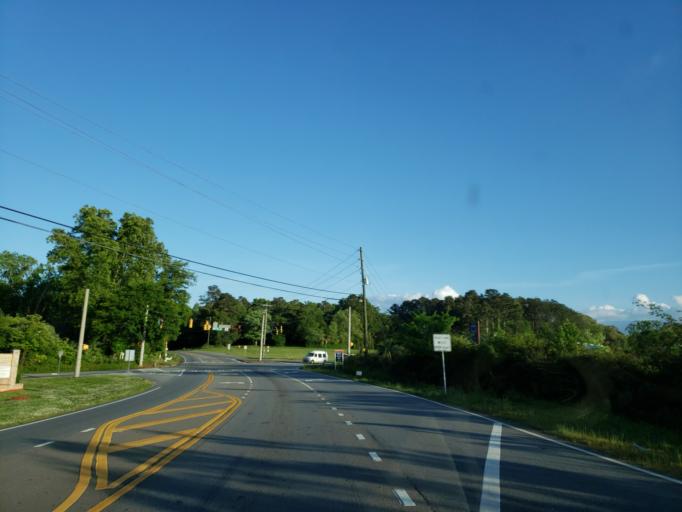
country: US
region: Georgia
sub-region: Cherokee County
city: Holly Springs
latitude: 34.2054
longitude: -84.5238
